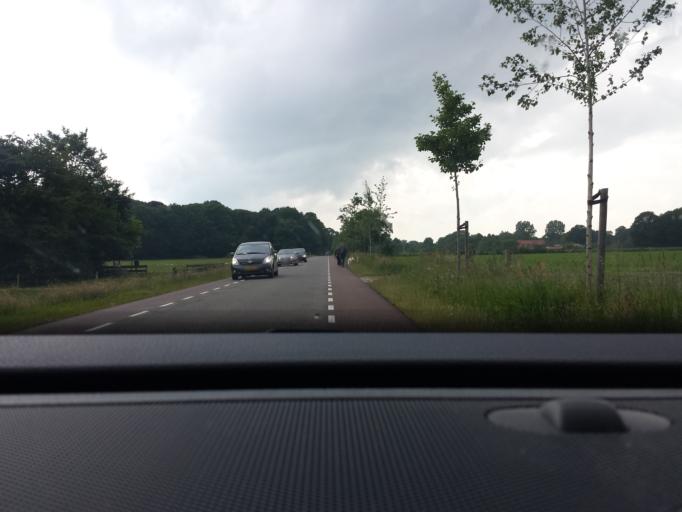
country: NL
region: Gelderland
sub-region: Berkelland
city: Eibergen
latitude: 52.0527
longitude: 6.6706
